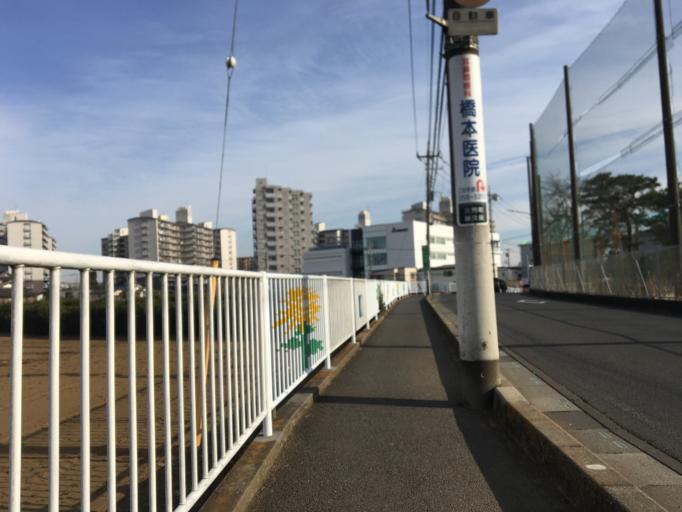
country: JP
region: Saitama
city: Oi
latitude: 35.8321
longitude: 139.5390
